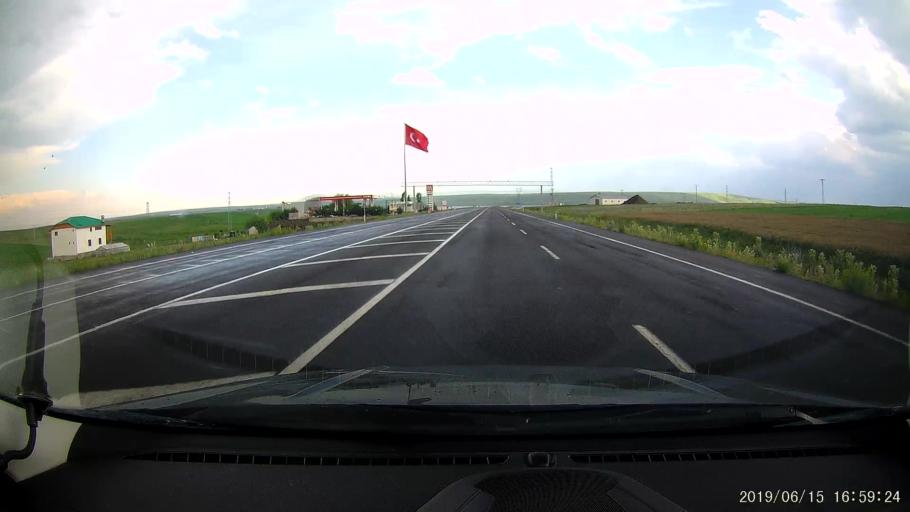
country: TR
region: Kars
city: Susuz
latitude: 40.7523
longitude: 43.1505
